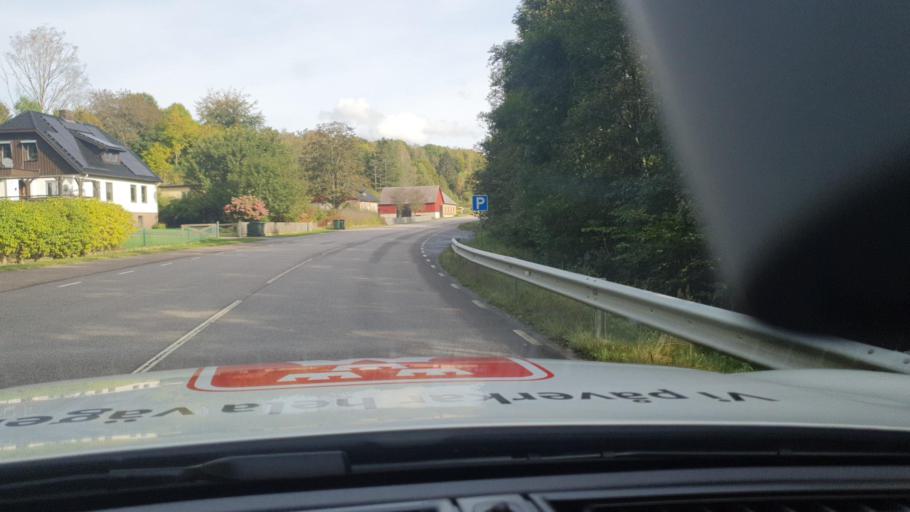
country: SE
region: Skane
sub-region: Bastads Kommun
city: Forslov
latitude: 56.3404
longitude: 12.8974
